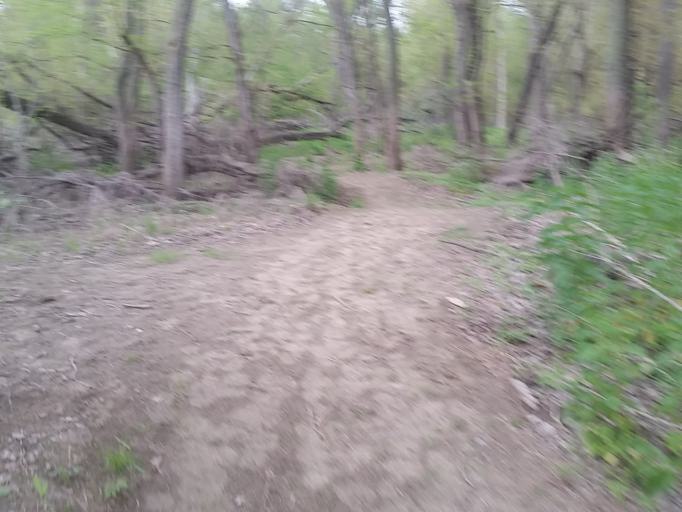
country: US
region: Nebraska
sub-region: Sarpy County
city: Bellevue
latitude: 41.1841
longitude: -95.8949
